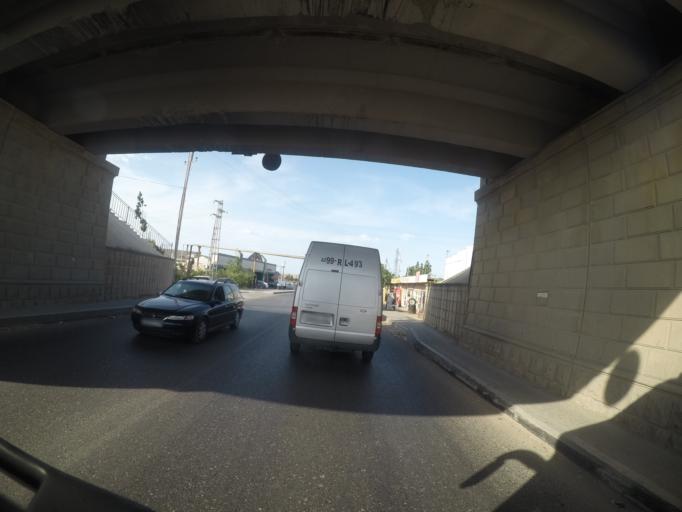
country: AZ
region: Baki
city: Bilajari
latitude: 40.4417
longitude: 49.7858
